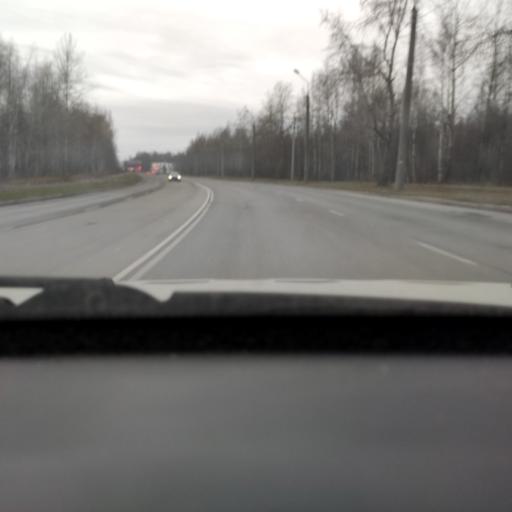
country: RU
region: Perm
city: Polazna
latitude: 58.1293
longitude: 56.4065
